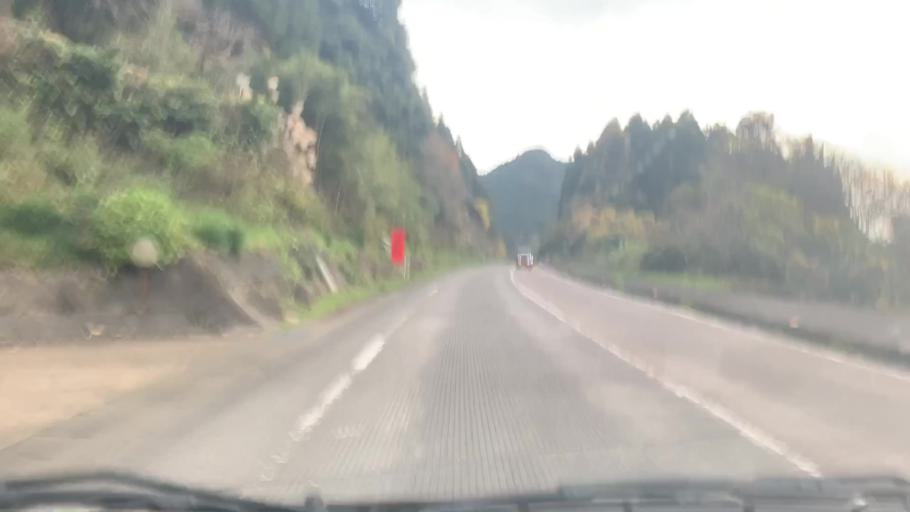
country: JP
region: Saga Prefecture
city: Kashima
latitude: 33.0553
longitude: 130.0717
